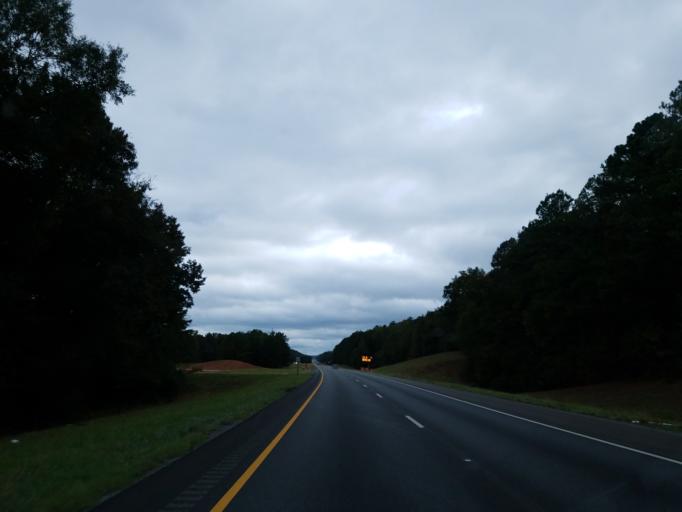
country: US
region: Alabama
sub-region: Hale County
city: Moundville
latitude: 33.0468
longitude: -87.7267
